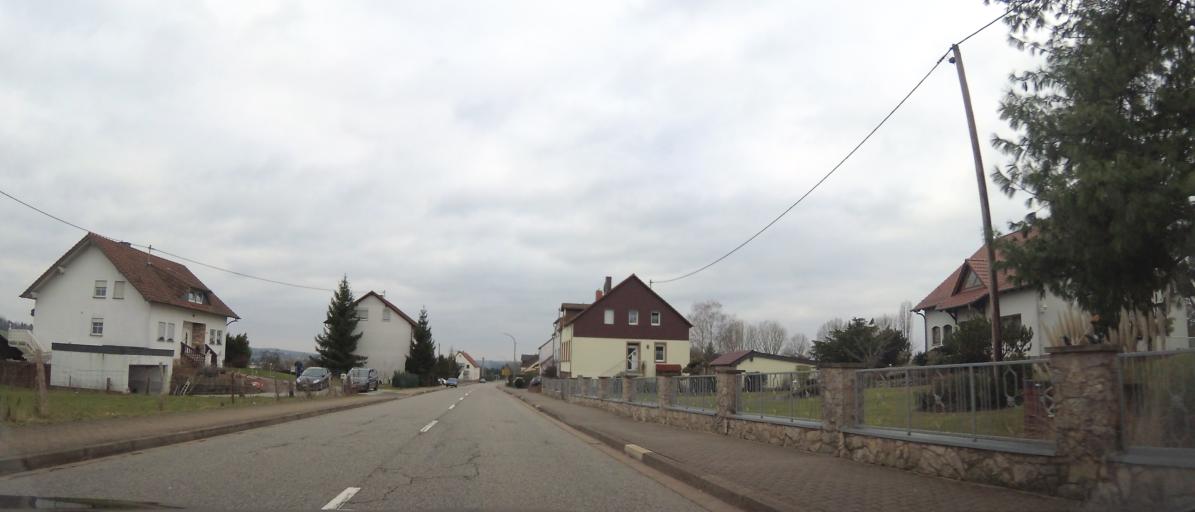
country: DE
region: Saarland
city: Heusweiler
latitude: 49.3396
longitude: 6.9489
